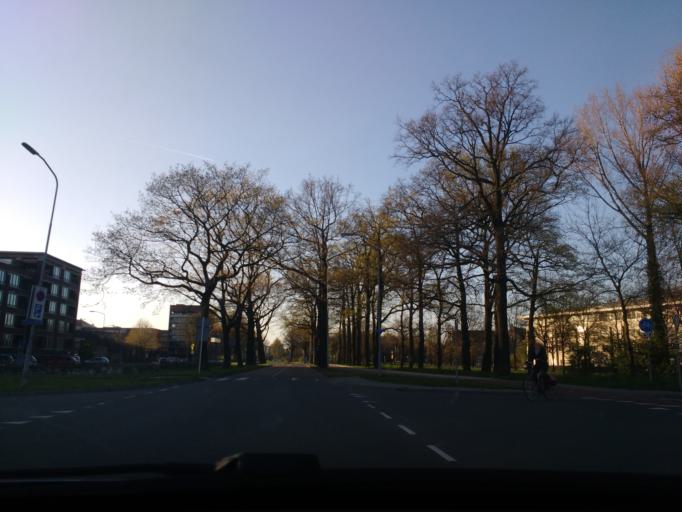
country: NL
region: Gelderland
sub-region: Gemeente Wageningen
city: Wageningen
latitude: 51.9656
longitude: 5.6583
